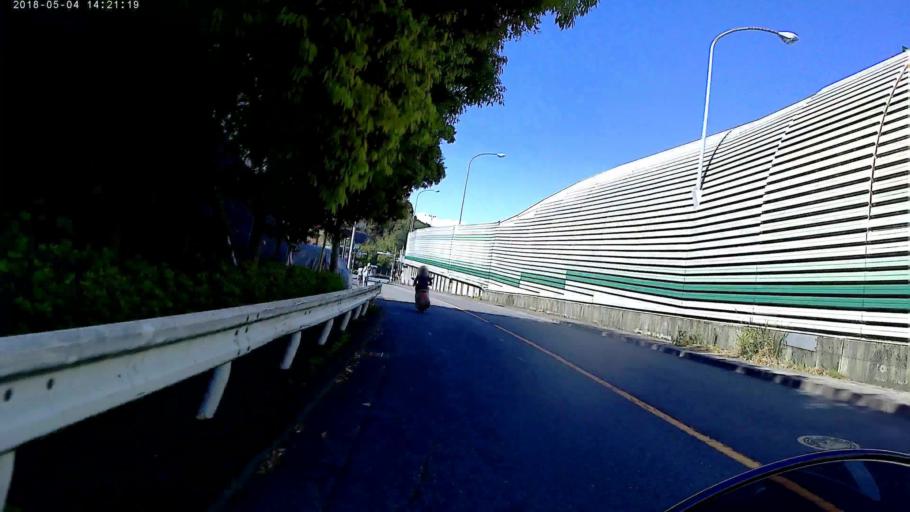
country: JP
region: Kanagawa
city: Yokohama
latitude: 35.4691
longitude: 139.5930
